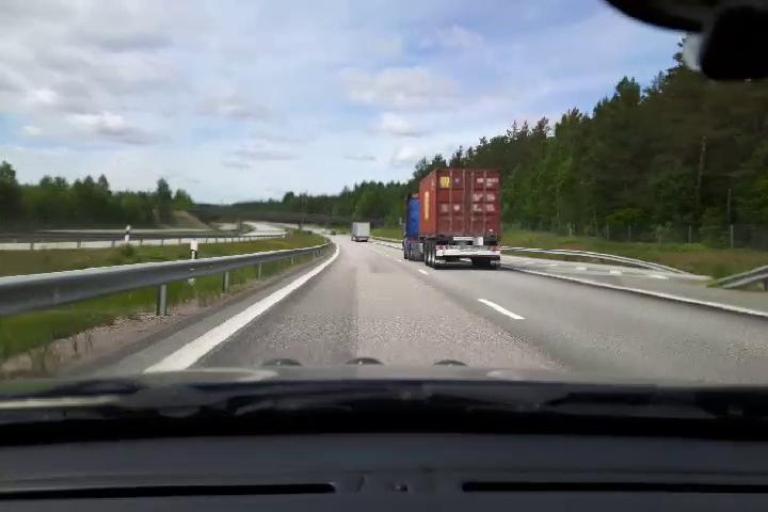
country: SE
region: Uppsala
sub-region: Alvkarleby Kommun
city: AElvkarleby
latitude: 60.4657
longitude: 17.4100
